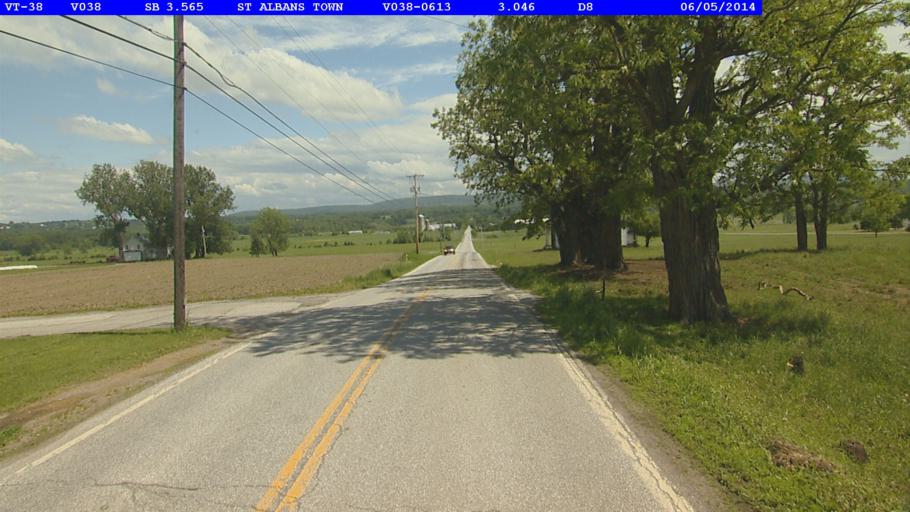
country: US
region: Vermont
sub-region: Franklin County
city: Swanton
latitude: 44.8536
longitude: -73.1322
